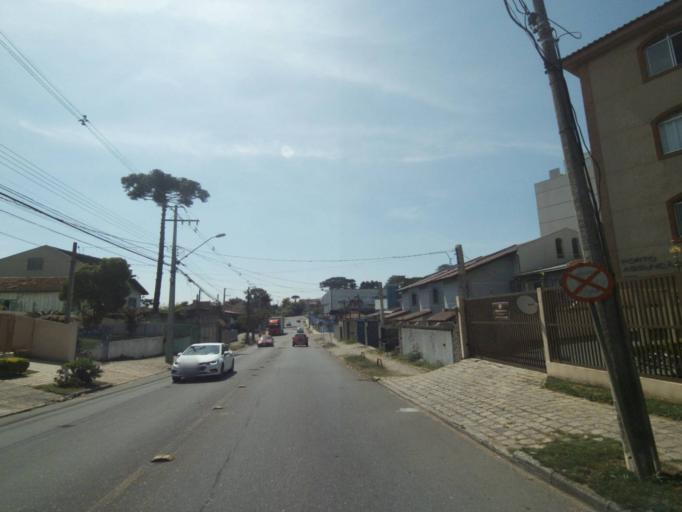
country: BR
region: Parana
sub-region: Curitiba
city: Curitiba
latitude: -25.4701
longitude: -49.3001
